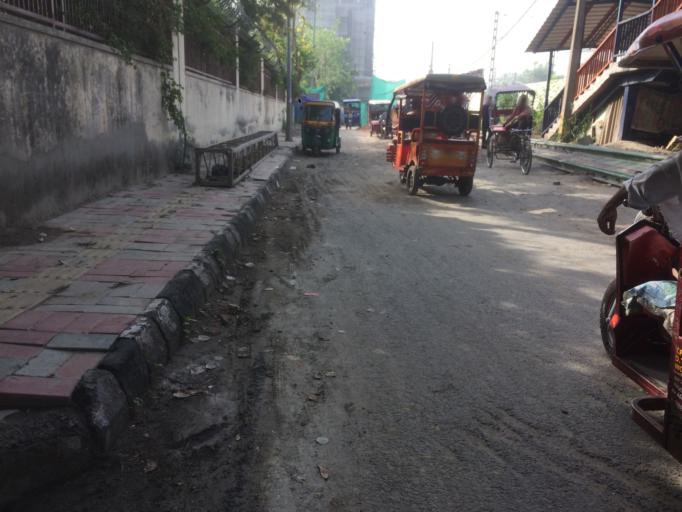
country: IN
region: NCT
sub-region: New Delhi
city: New Delhi
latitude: 28.6280
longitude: 77.2383
